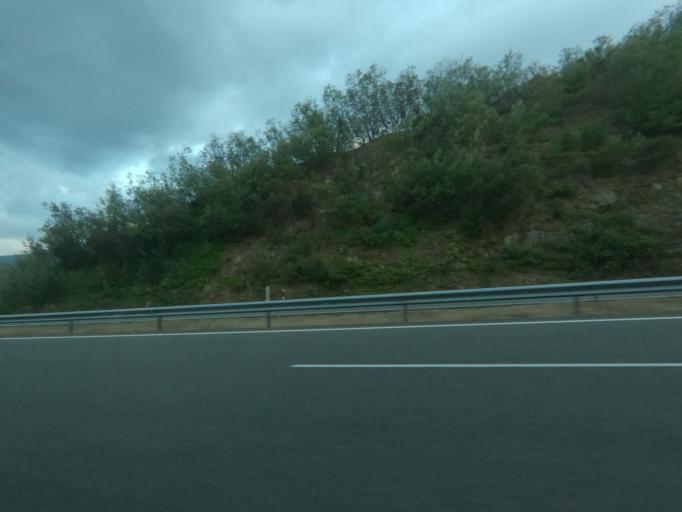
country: ES
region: Galicia
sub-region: Provincia de Ourense
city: Ribadavia
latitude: 42.3052
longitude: -8.1509
